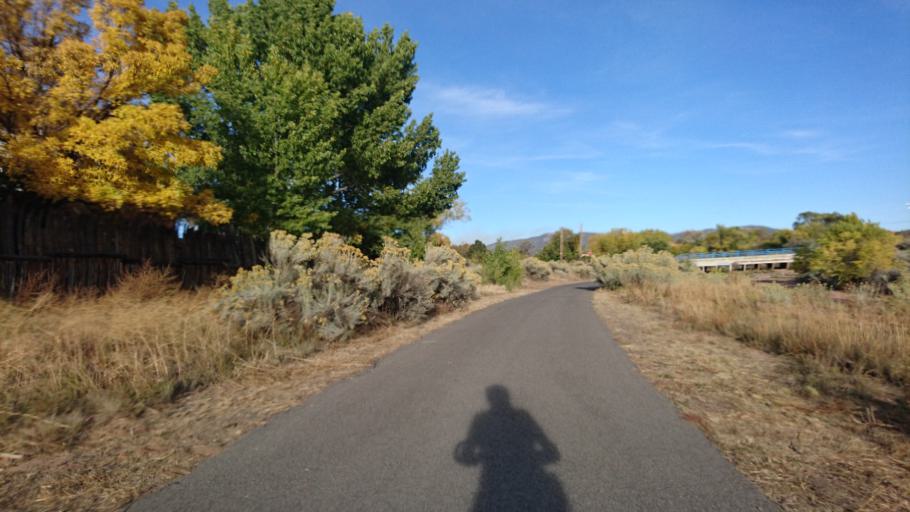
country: US
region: New Mexico
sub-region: Santa Fe County
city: Agua Fria
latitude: 35.6455
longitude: -105.9755
